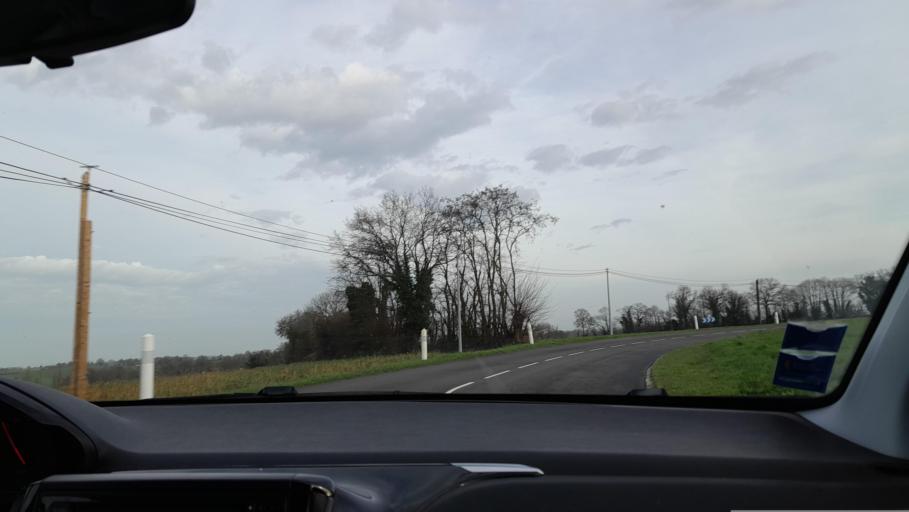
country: FR
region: Brittany
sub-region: Departement d'Ille-et-Vilaine
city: La Guerche-de-Bretagne
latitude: 47.9558
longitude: -1.1770
